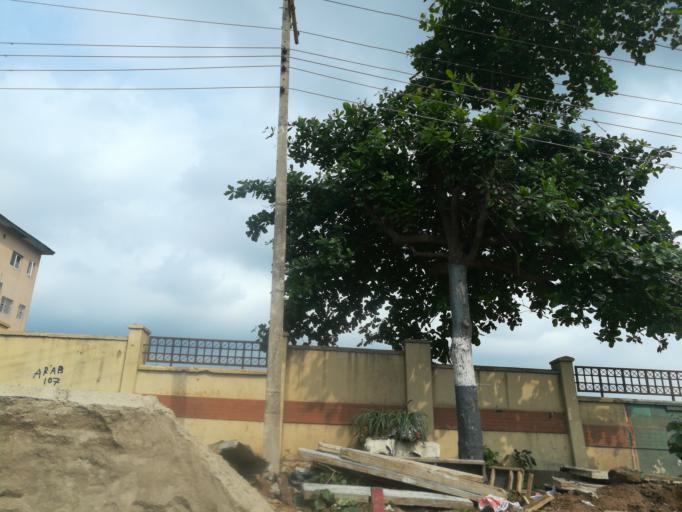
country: NG
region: Lagos
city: Agege
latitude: 6.6253
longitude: 3.3534
